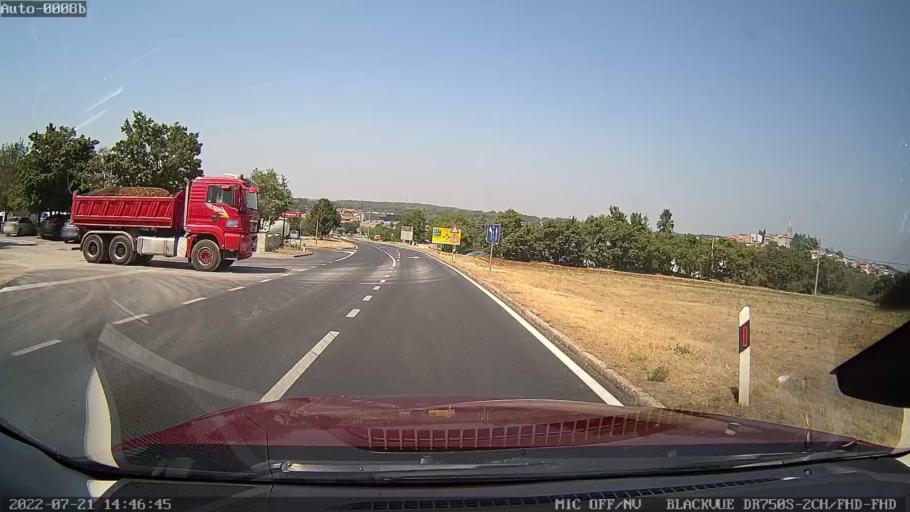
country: HR
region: Istarska
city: Pazin
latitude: 45.1392
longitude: 13.9011
